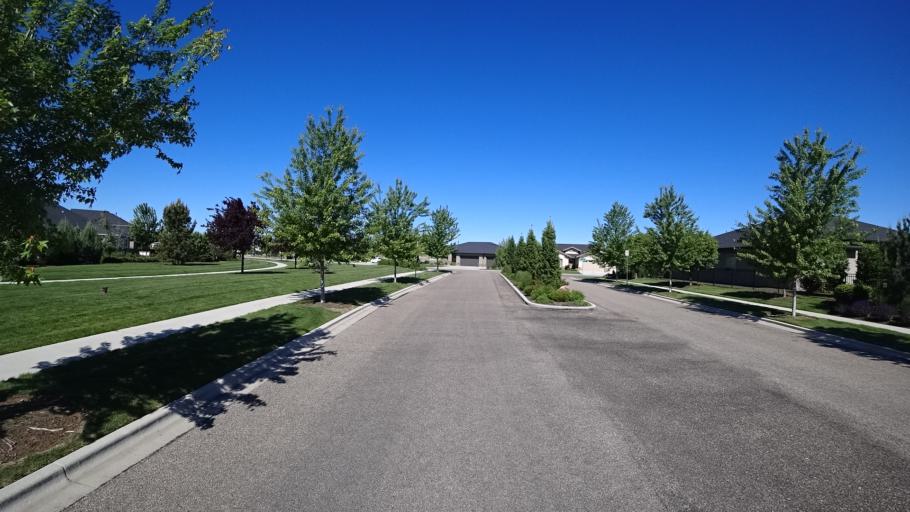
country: US
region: Idaho
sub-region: Ada County
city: Eagle
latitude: 43.6676
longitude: -116.3985
